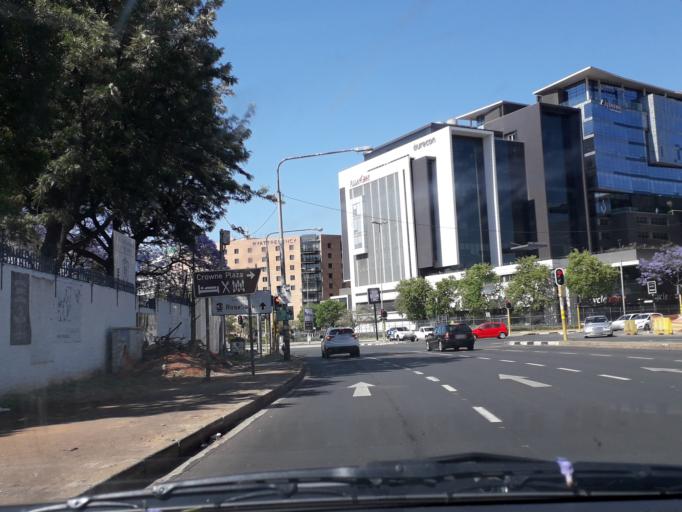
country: ZA
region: Gauteng
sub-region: City of Johannesburg Metropolitan Municipality
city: Johannesburg
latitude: -26.1415
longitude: 28.0439
